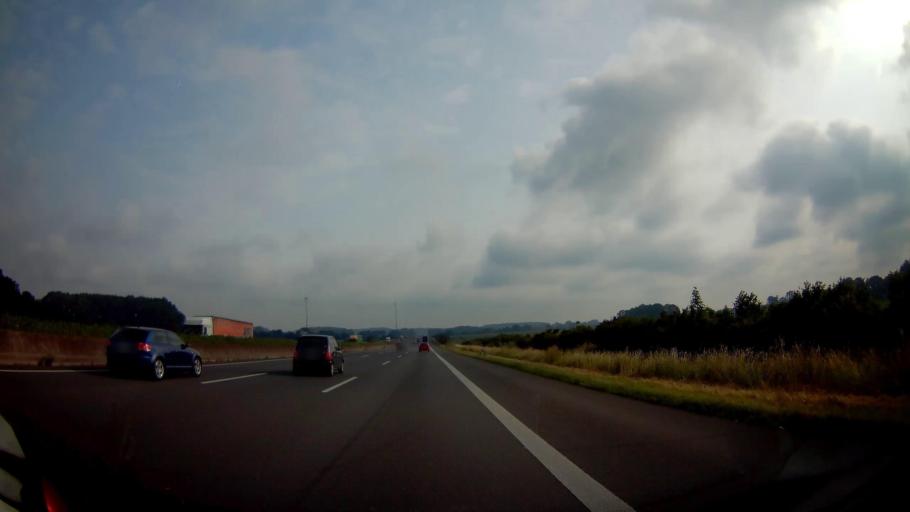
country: DE
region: North Rhine-Westphalia
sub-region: Regierungsbezirk Munster
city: Beckum
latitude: 51.7492
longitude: 7.9953
